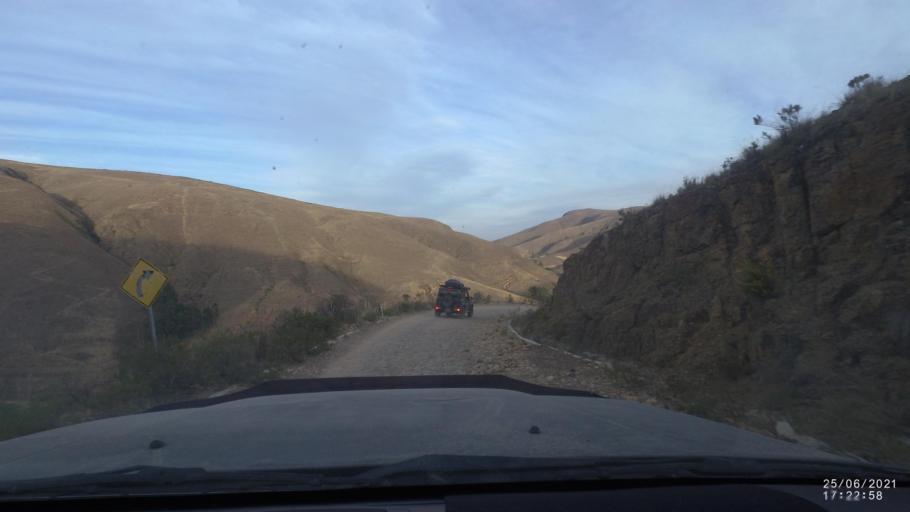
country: BO
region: Cochabamba
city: Mizque
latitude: -17.9112
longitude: -65.6860
